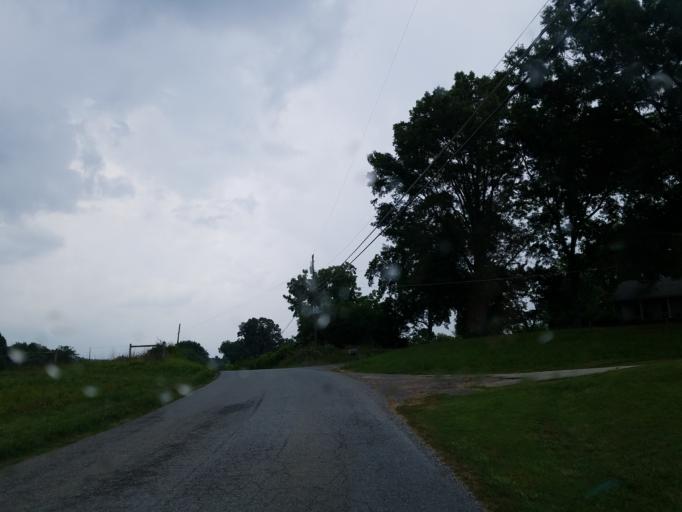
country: US
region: Georgia
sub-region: Bartow County
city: Rydal
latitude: 34.2745
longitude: -84.7551
